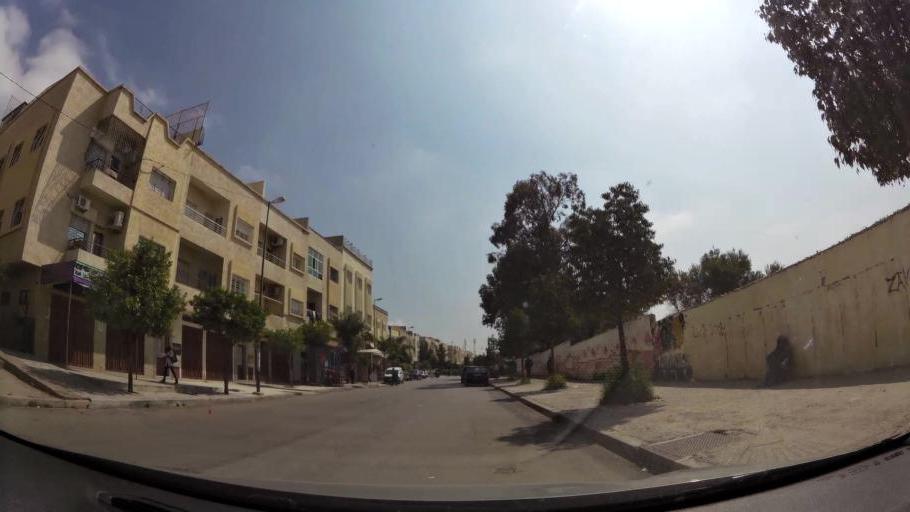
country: MA
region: Fes-Boulemane
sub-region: Fes
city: Fes
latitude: 34.0587
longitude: -5.0204
